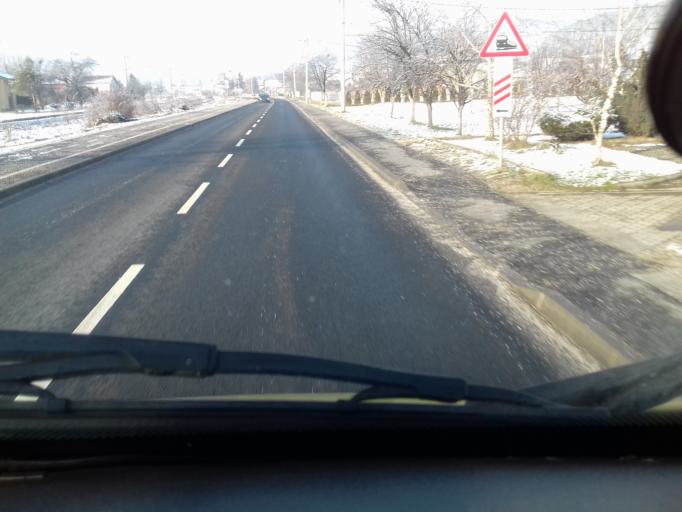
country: BA
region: Federation of Bosnia and Herzegovina
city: Mahala
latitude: 43.9813
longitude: 18.2398
